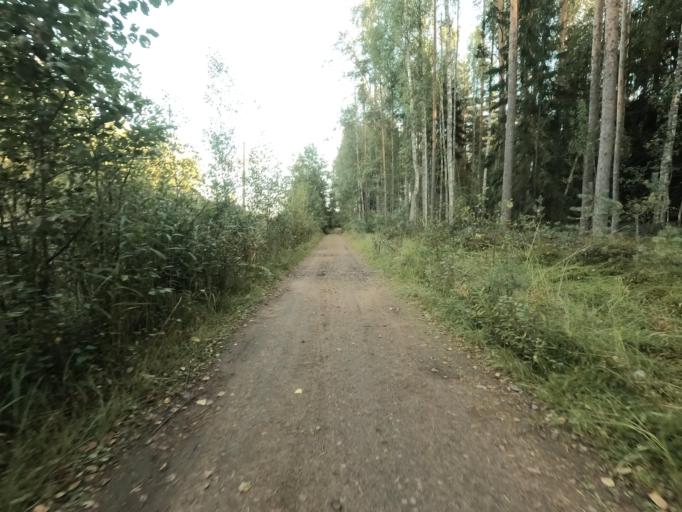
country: RU
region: Leningrad
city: Otradnoye
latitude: 59.8418
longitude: 30.7768
